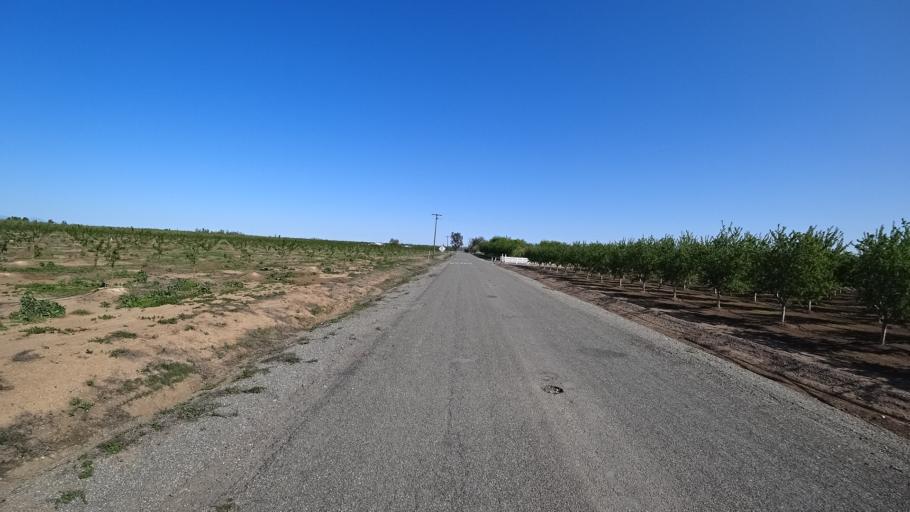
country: US
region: California
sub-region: Glenn County
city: Hamilton City
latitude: 39.7676
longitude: -122.0477
